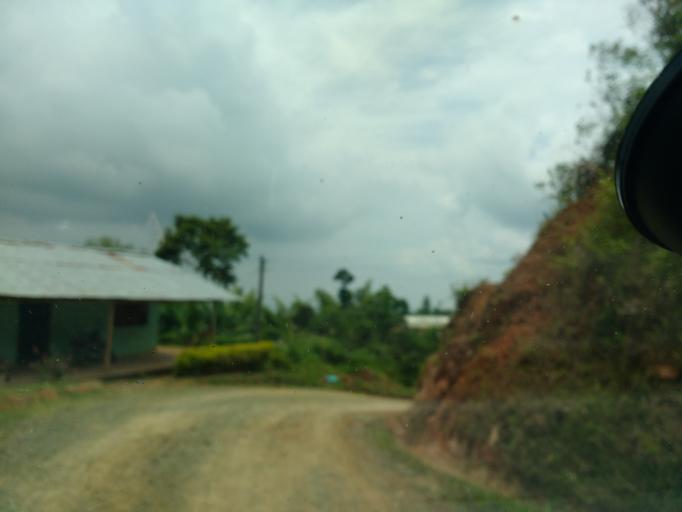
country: CO
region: Cauca
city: Santander de Quilichao
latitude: 2.9219
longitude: -76.4671
